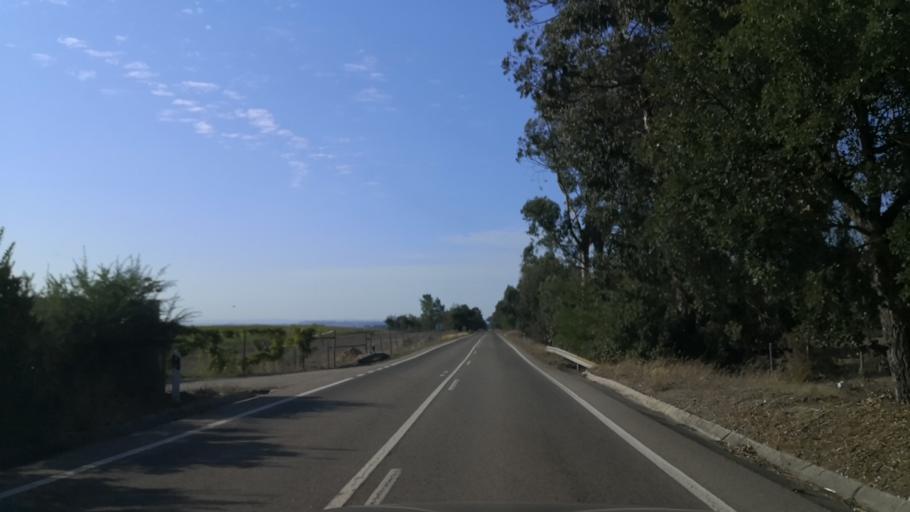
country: PT
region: Santarem
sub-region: Almeirim
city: Fazendas de Almeirim
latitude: 39.1364
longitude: -8.6104
